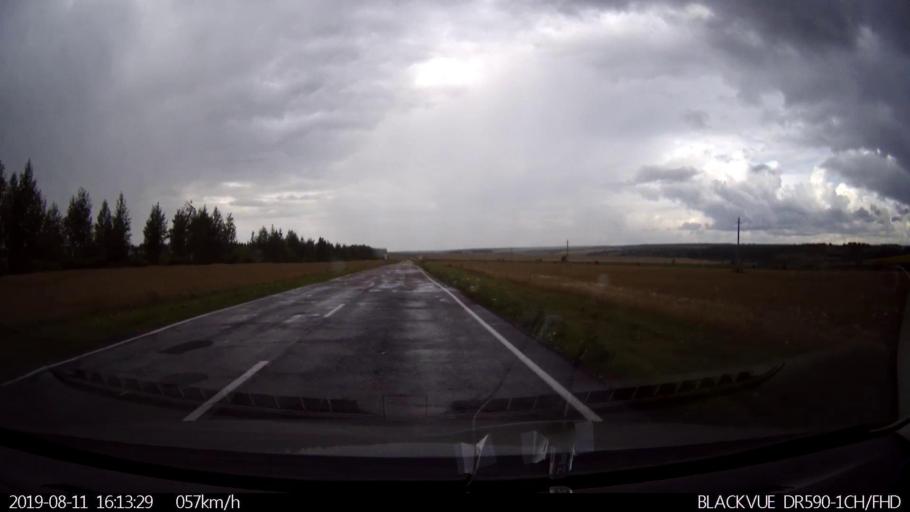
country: RU
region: Ulyanovsk
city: Ignatovka
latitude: 54.0206
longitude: 47.6367
